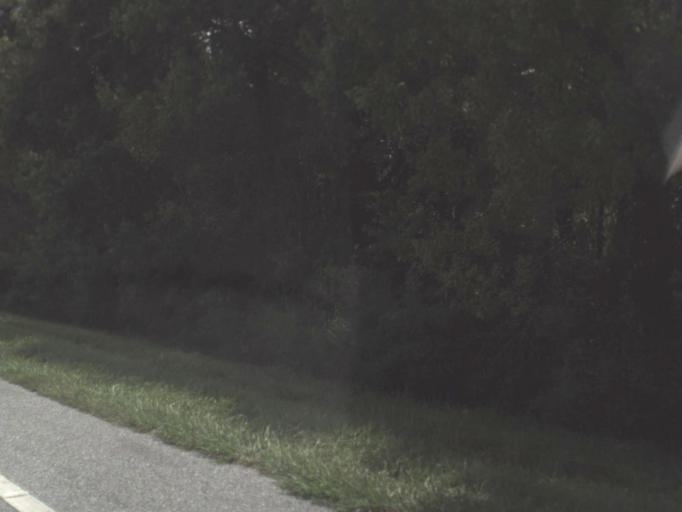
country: US
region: Florida
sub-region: Sarasota County
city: Lake Sarasota
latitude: 27.3397
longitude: -82.1463
